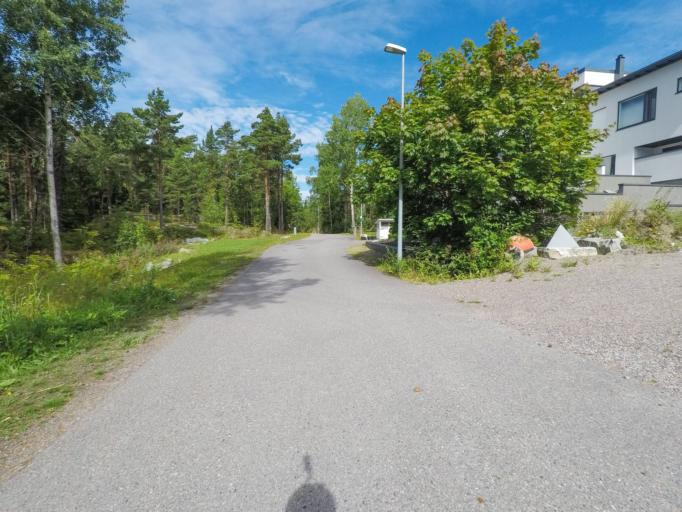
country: FI
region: Uusimaa
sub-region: Helsinki
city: Vantaa
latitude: 60.1621
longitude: 25.0887
